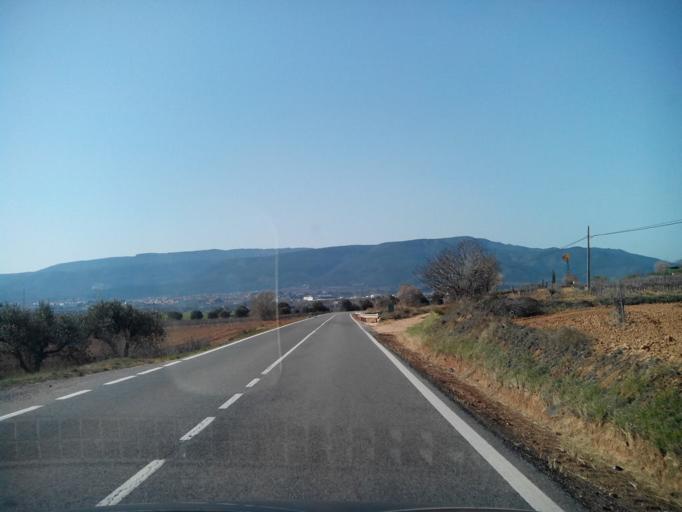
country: ES
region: Catalonia
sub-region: Provincia de Tarragona
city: Montblanc
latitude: 41.3994
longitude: 1.1865
